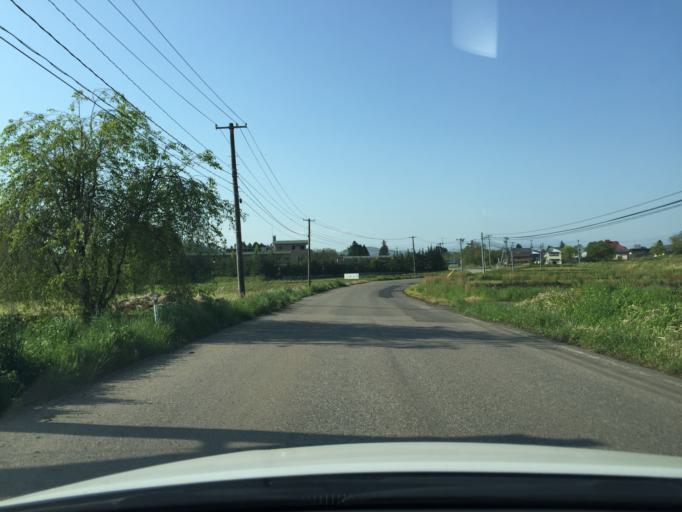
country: JP
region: Fukushima
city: Kitakata
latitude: 37.6571
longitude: 139.7746
